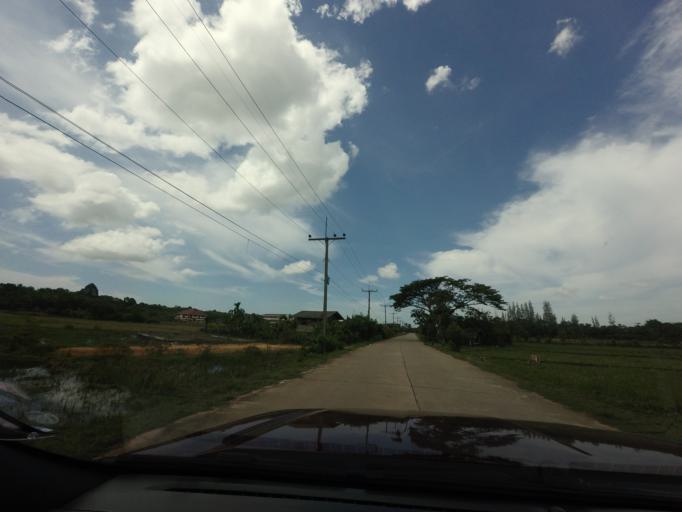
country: TH
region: Narathiwat
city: Bacho
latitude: 6.4869
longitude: 101.6623
